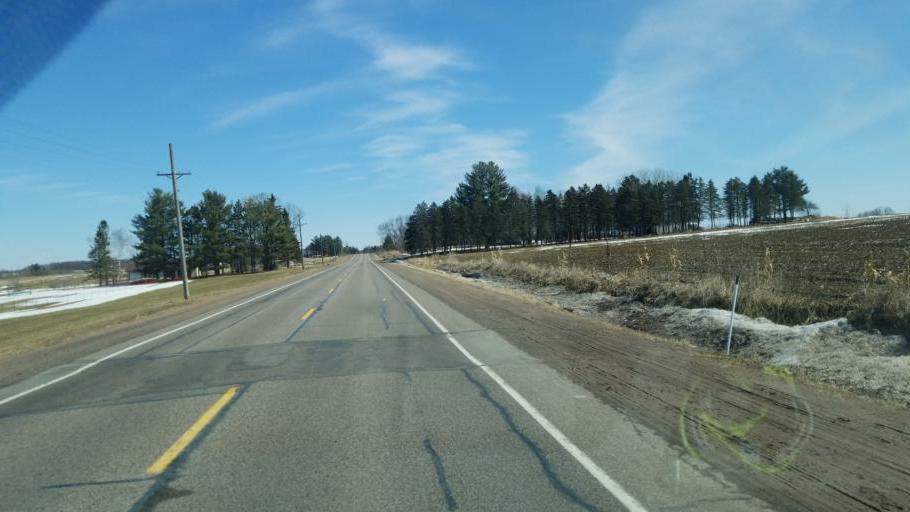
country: US
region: Wisconsin
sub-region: Clark County
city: Loyal
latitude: 44.5827
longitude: -90.3901
